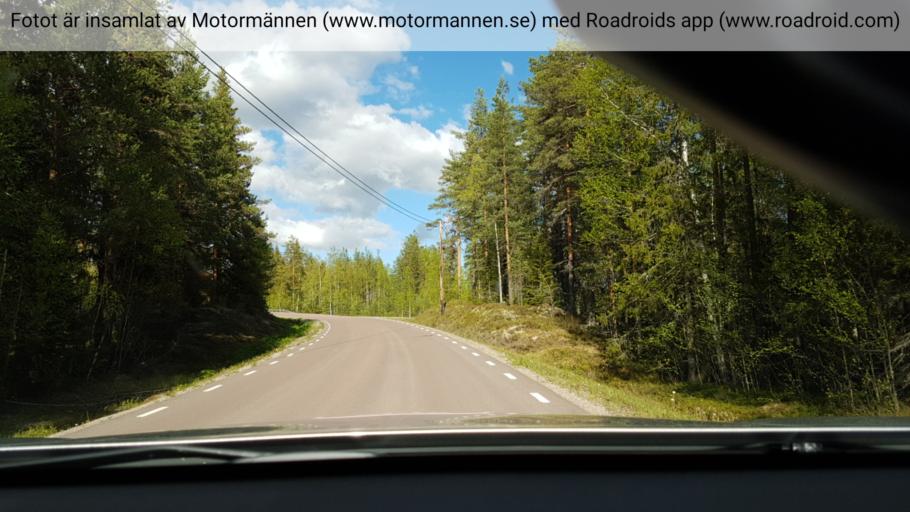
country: SE
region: Dalarna
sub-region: Rattviks Kommun
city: Raettvik
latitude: 60.7821
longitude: 15.2387
